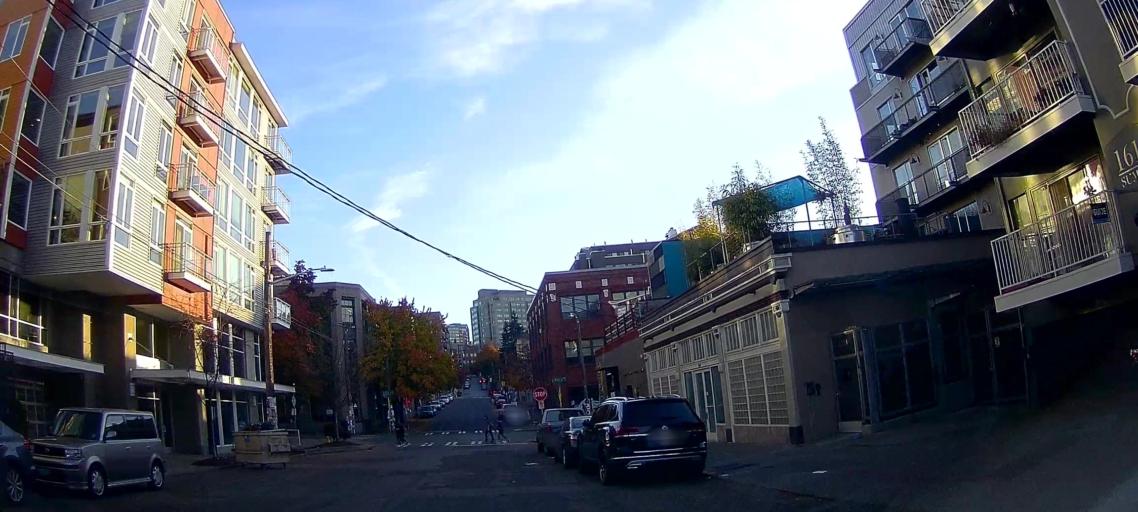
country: US
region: Washington
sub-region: King County
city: Seattle
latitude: 47.6157
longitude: -122.3255
